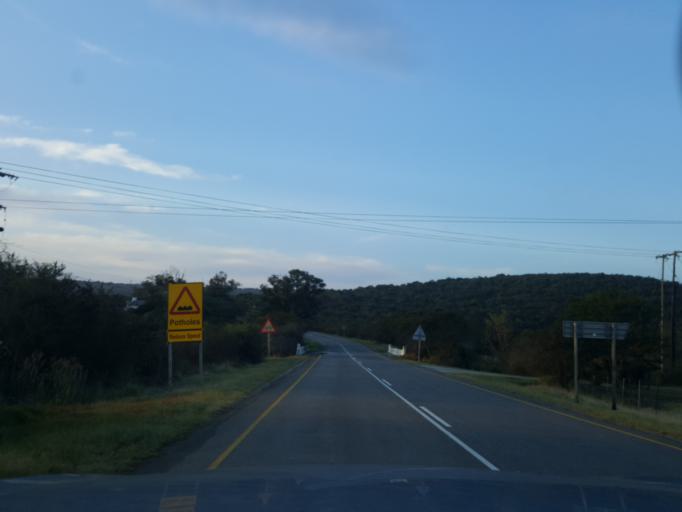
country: ZA
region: Eastern Cape
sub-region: Cacadu District Municipality
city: Grahamstown
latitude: -33.4694
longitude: 26.4807
